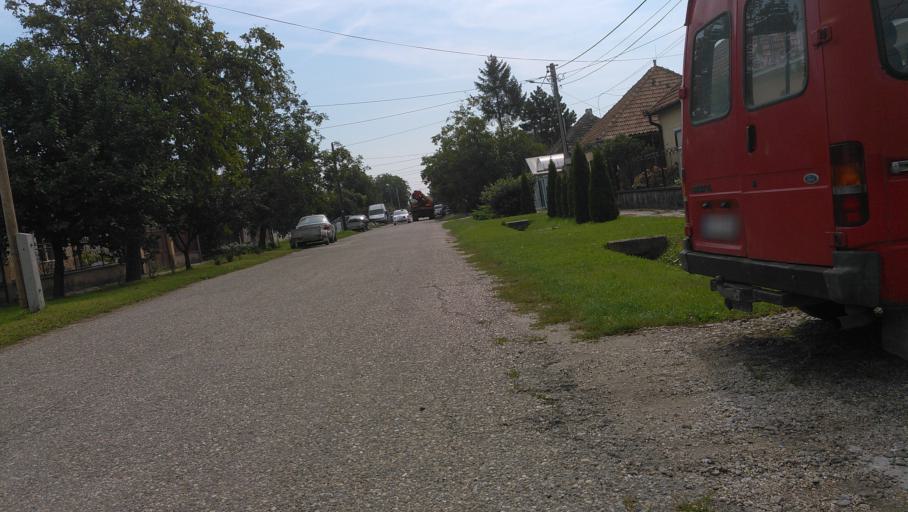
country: SK
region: Nitriansky
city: Kolarovo
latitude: 47.9093
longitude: 17.9923
